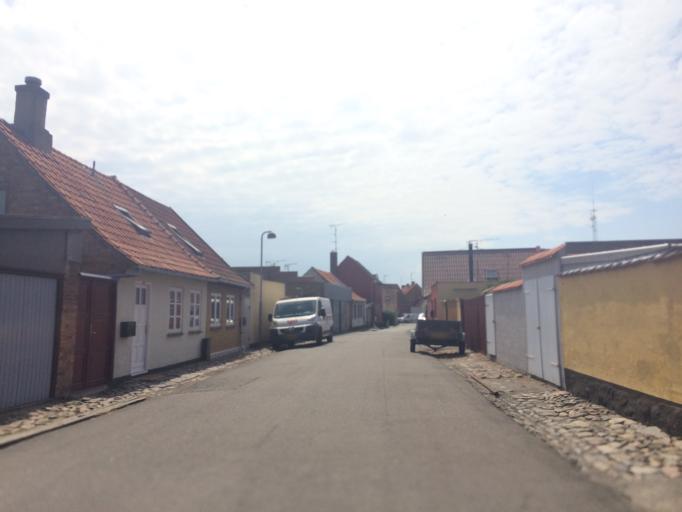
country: DK
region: Capital Region
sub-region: Bornholm Kommune
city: Ronne
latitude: 55.1061
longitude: 14.7000
